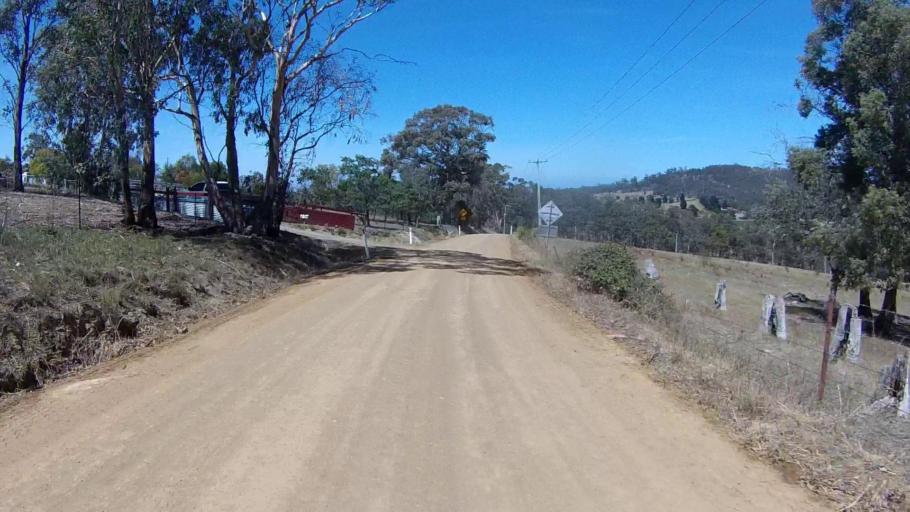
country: AU
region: Tasmania
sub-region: Sorell
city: Sorell
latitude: -42.7819
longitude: 147.6444
